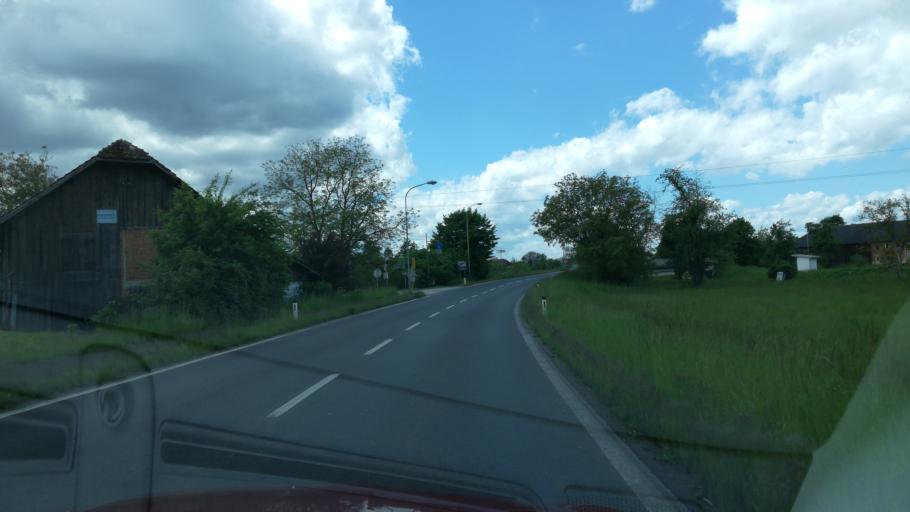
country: AT
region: Upper Austria
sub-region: Politischer Bezirk Linz-Land
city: Ansfelden
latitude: 48.1994
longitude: 14.2682
